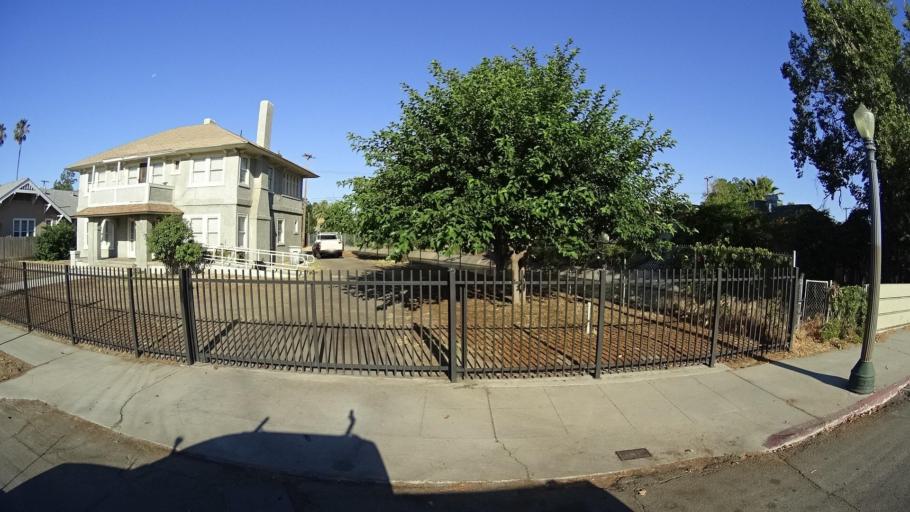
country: US
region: California
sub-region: Fresno County
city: Fresno
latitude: 36.7485
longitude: -119.8031
